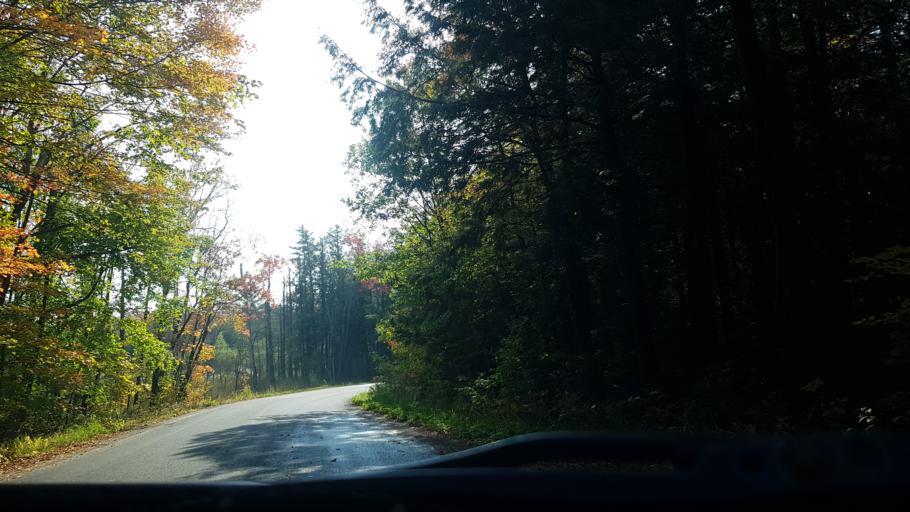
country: CA
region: Ontario
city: Bracebridge
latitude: 44.9742
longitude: -79.2592
